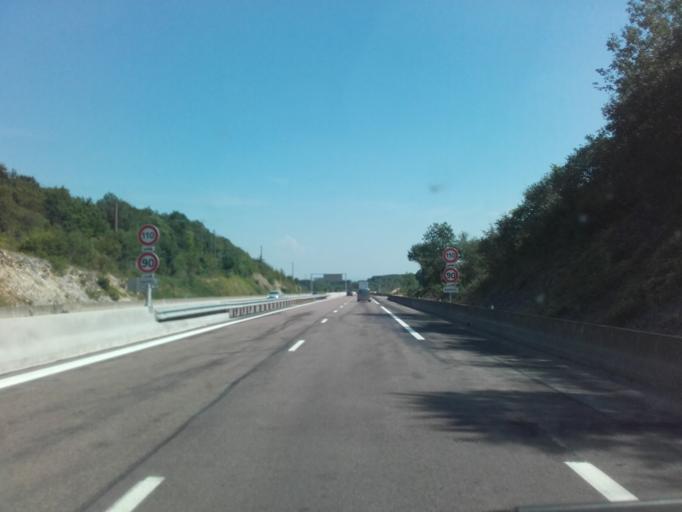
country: FR
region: Bourgogne
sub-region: Departement de la Cote-d'Or
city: Savigny-les-Beaune
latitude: 47.0986
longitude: 4.7442
